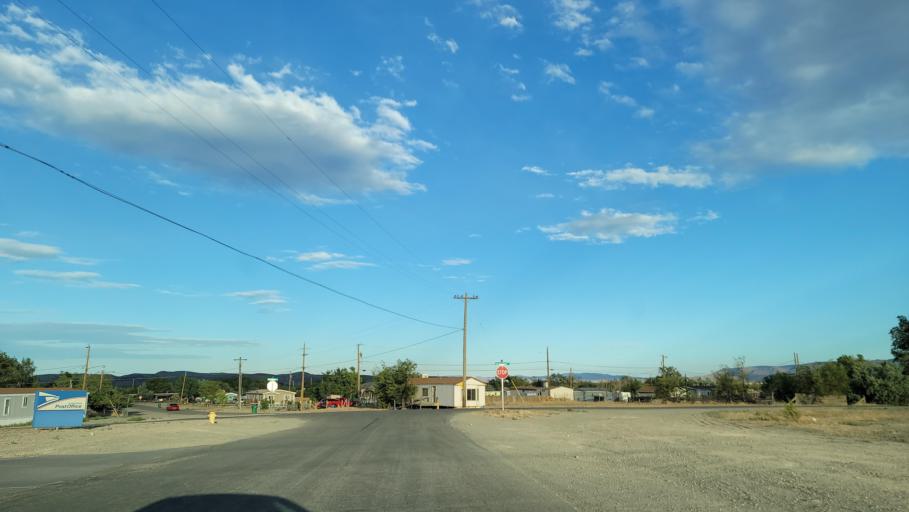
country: US
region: Nevada
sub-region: Lyon County
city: Silver Springs
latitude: 39.4145
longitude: -119.2241
